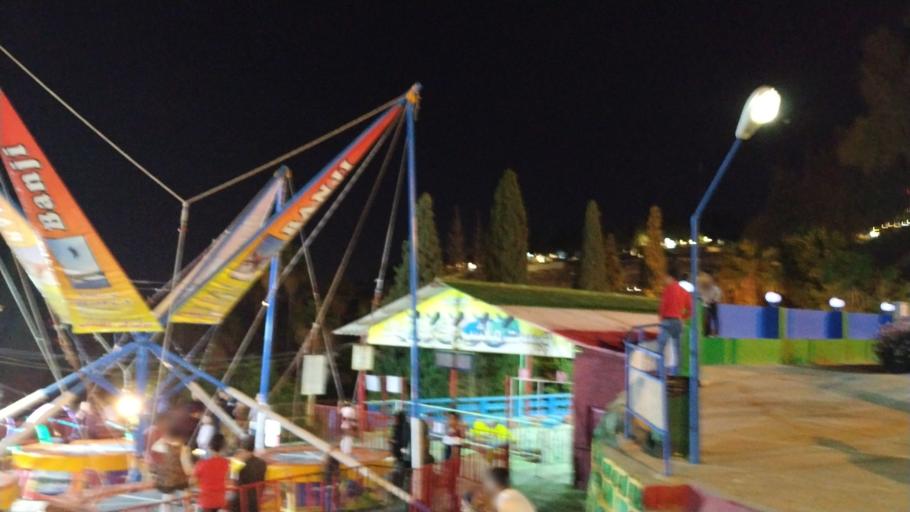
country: IR
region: Fars
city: Shiraz
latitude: 29.6355
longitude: 52.5580
